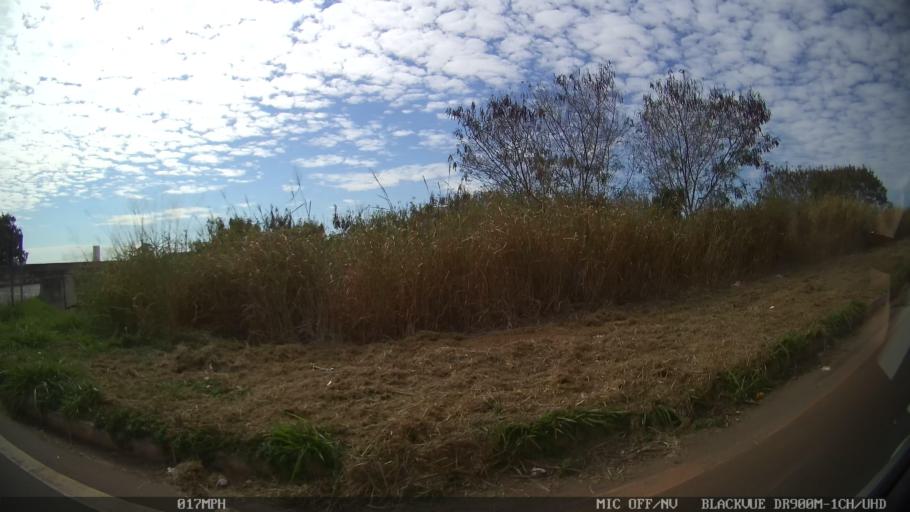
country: BR
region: Sao Paulo
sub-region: Santa Barbara D'Oeste
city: Santa Barbara d'Oeste
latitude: -22.7611
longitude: -47.4618
